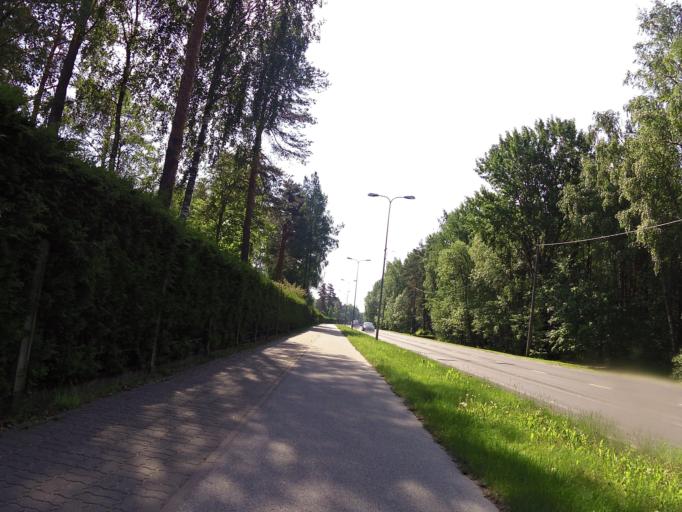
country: EE
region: Harju
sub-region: Harku vald
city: Tabasalu
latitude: 59.4431
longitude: 24.6166
